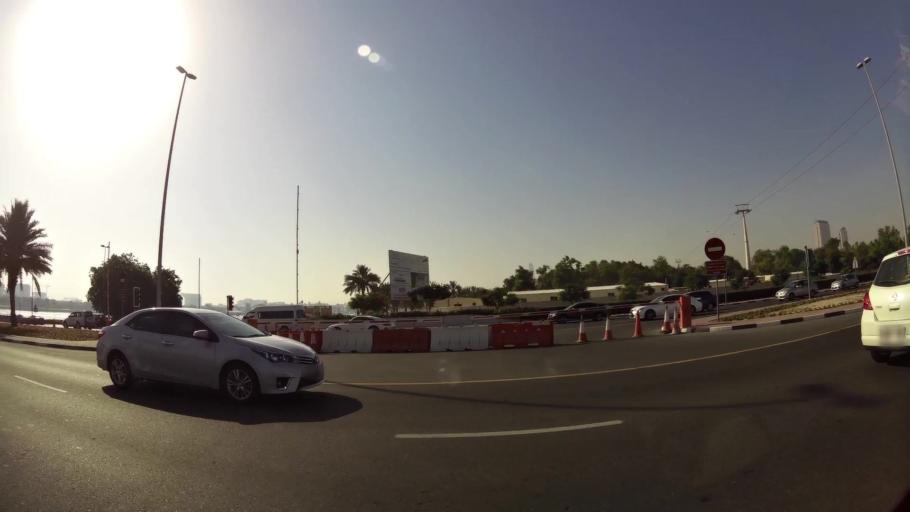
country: AE
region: Ash Shariqah
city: Sharjah
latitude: 25.2474
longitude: 55.3239
